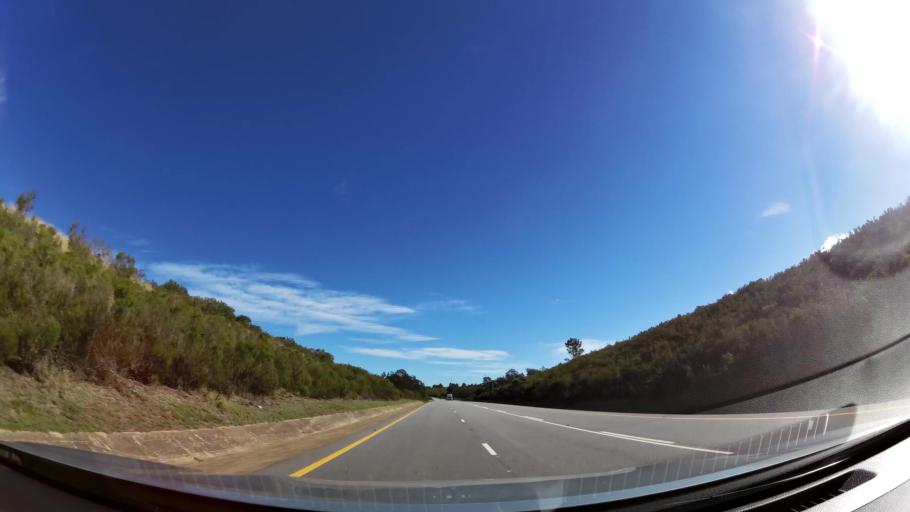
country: ZA
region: Eastern Cape
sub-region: Cacadu District Municipality
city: Kruisfontein
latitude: -34.0155
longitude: 24.6293
